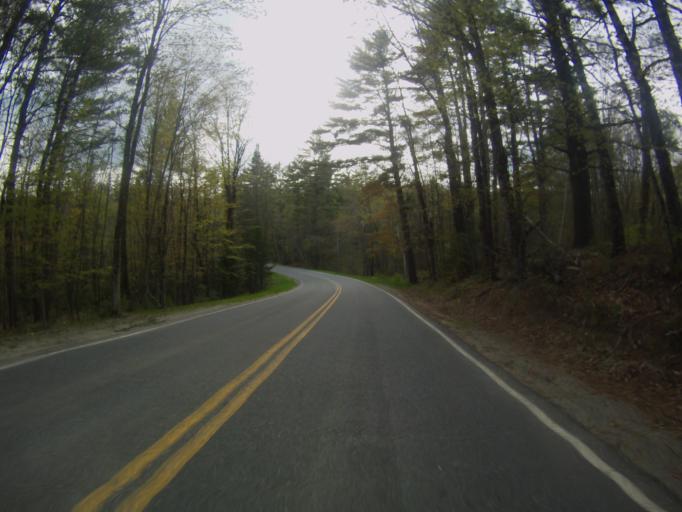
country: US
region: New York
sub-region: Warren County
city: Warrensburg
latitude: 43.8426
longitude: -73.8705
